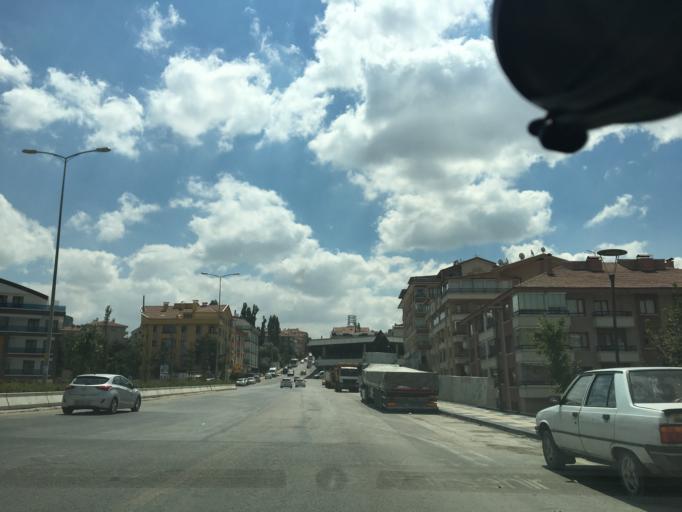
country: TR
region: Ankara
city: Ankara
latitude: 39.8840
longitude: 32.8305
